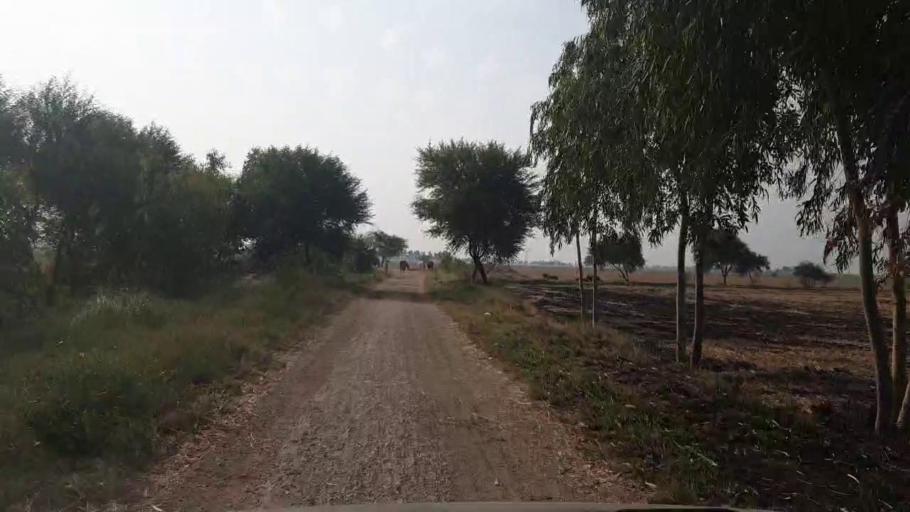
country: PK
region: Sindh
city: Tando Muhammad Khan
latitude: 25.1031
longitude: 68.5016
